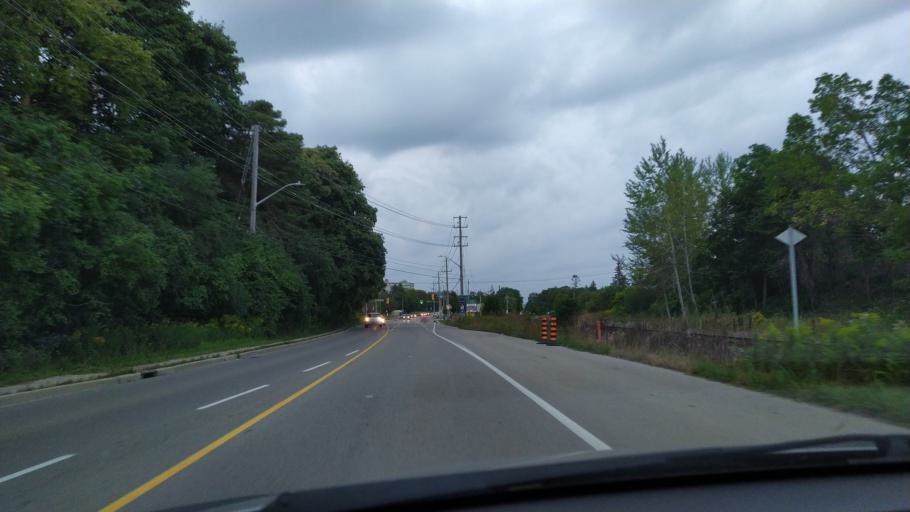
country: CA
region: Ontario
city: Kitchener
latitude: 43.4249
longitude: -80.4170
